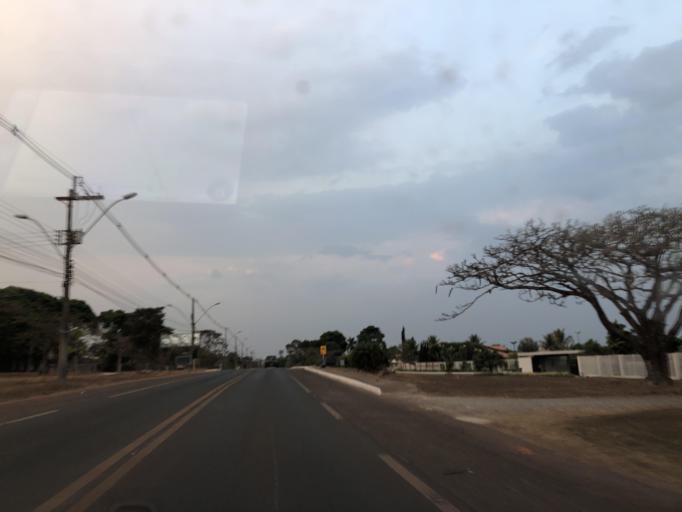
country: BR
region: Federal District
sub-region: Brasilia
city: Brasilia
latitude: -15.9222
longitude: -47.9495
